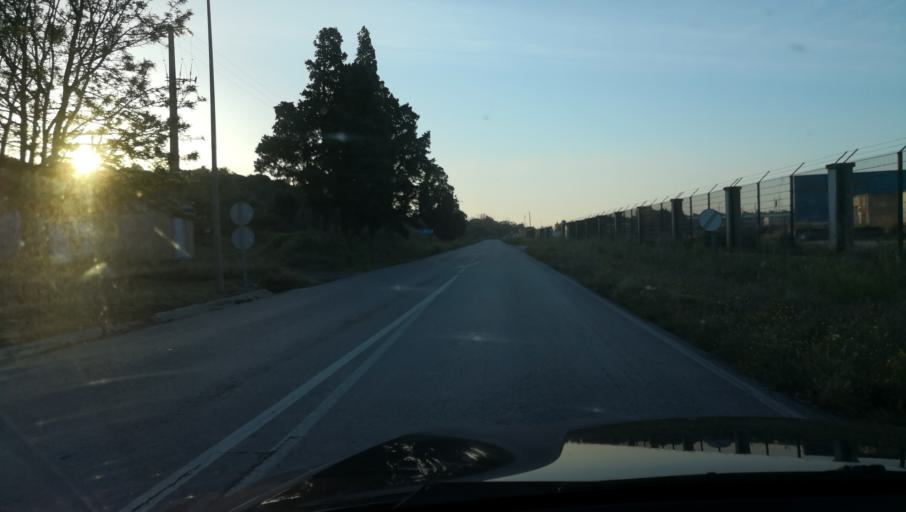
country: PT
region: Setubal
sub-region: Setubal
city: Setubal
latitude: 38.4928
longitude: -8.8264
